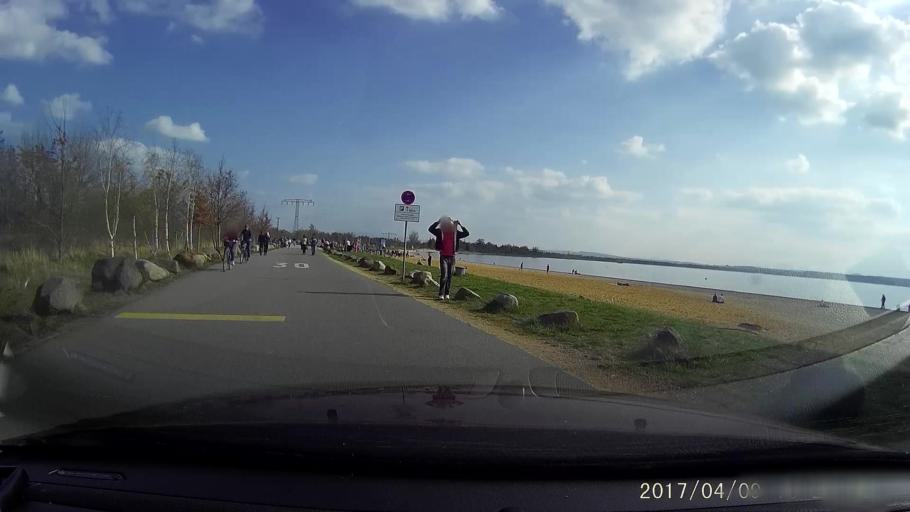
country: DE
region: Saxony
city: Goerlitz
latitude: 51.1074
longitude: 14.9746
